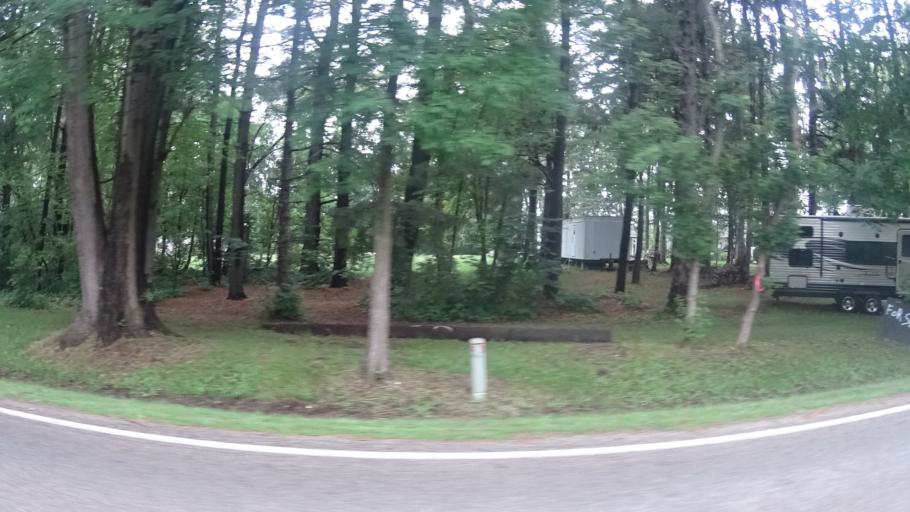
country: US
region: Ohio
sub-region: Erie County
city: Huron
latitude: 41.3467
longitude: -82.5557
